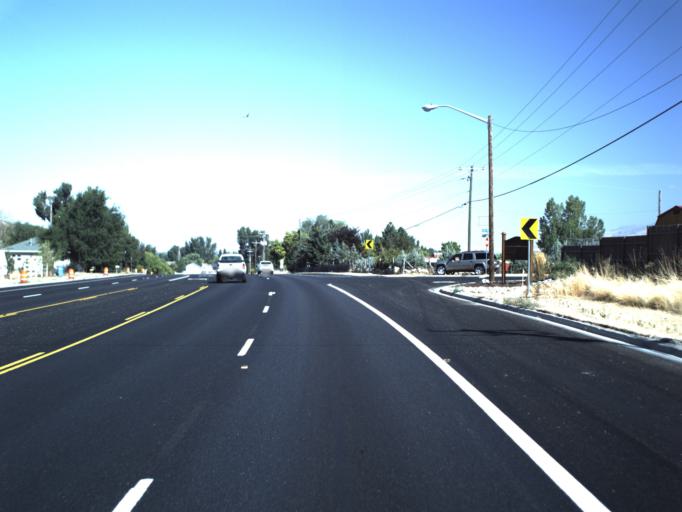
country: US
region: Utah
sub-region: Cache County
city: Nibley
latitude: 41.6578
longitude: -111.8328
